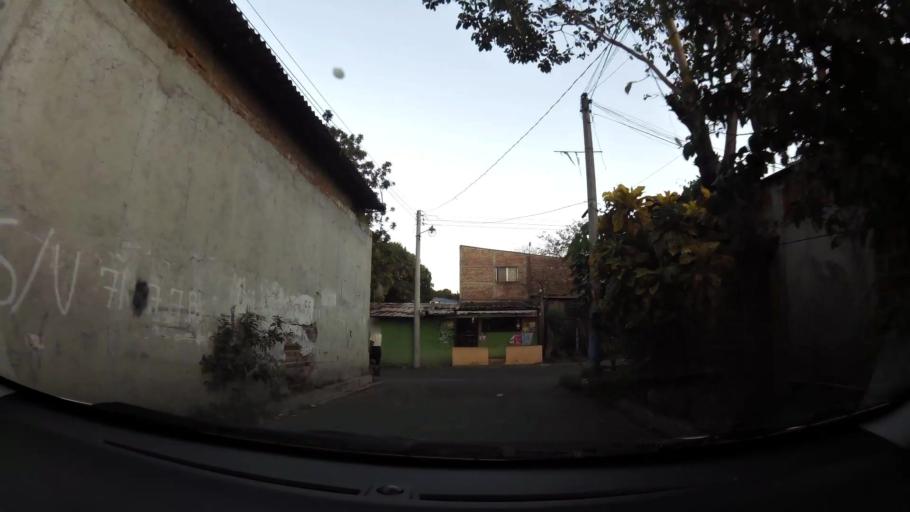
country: SV
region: Sonsonate
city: Armenia
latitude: 13.7351
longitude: -89.3850
